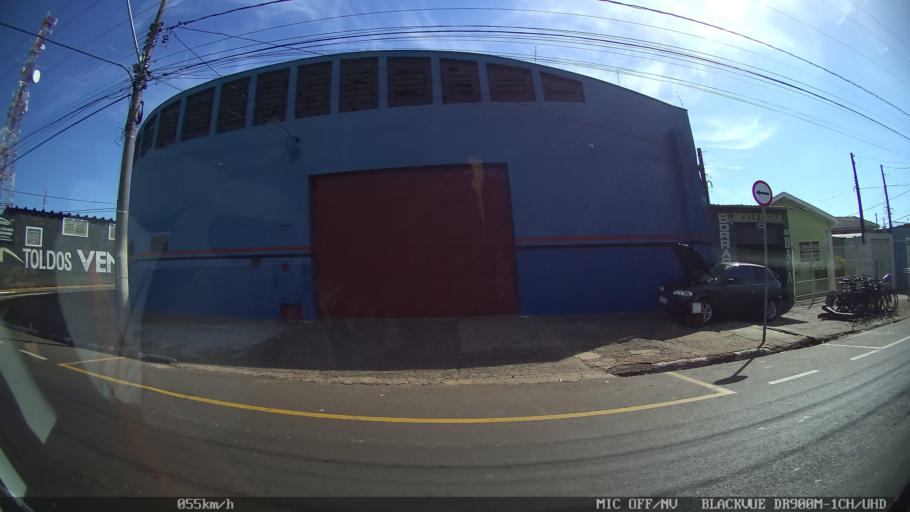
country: BR
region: Sao Paulo
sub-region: Franca
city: Franca
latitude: -20.5035
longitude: -47.3992
